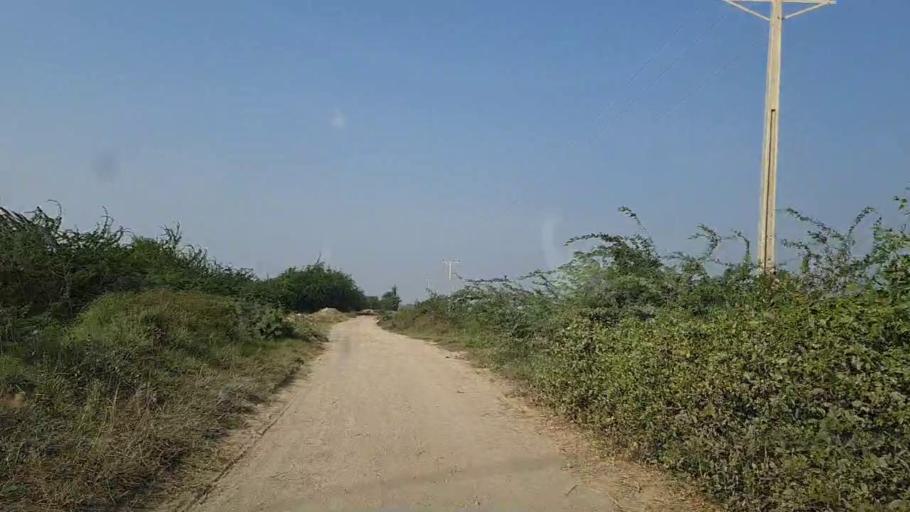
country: PK
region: Sindh
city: Mirpur Sakro
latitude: 24.5808
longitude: 67.5678
